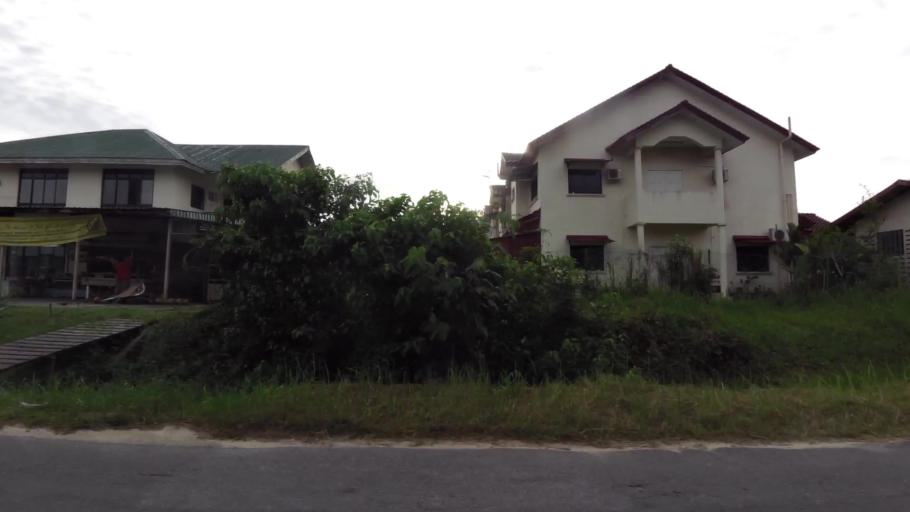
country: BN
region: Brunei and Muara
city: Bandar Seri Begawan
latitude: 4.9143
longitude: 114.8945
